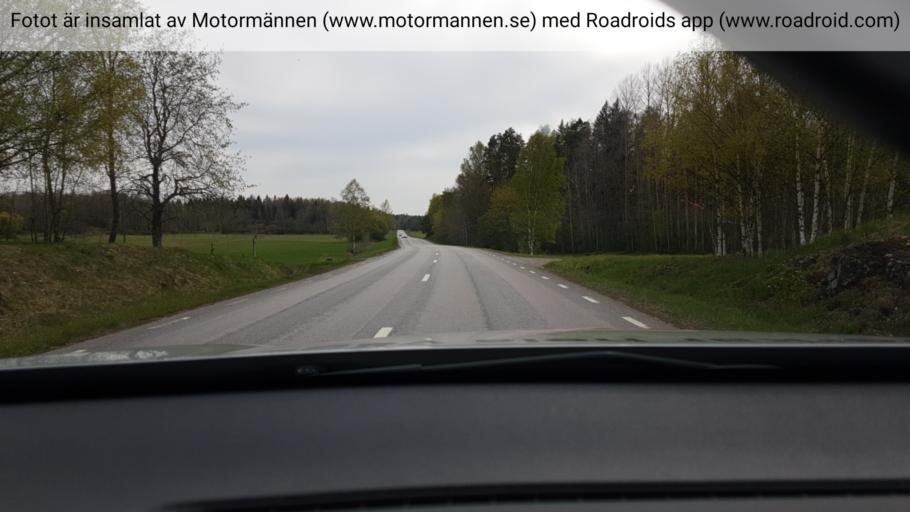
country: SE
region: Stockholm
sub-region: Norrtalje Kommun
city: Nykvarn
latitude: 59.9269
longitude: 18.1107
